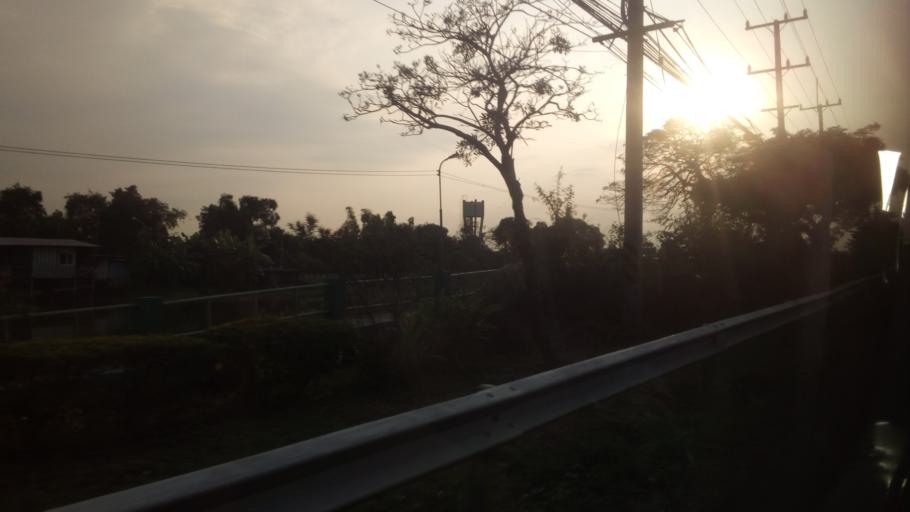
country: TH
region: Pathum Thani
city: Thanyaburi
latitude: 13.9980
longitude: 100.6775
